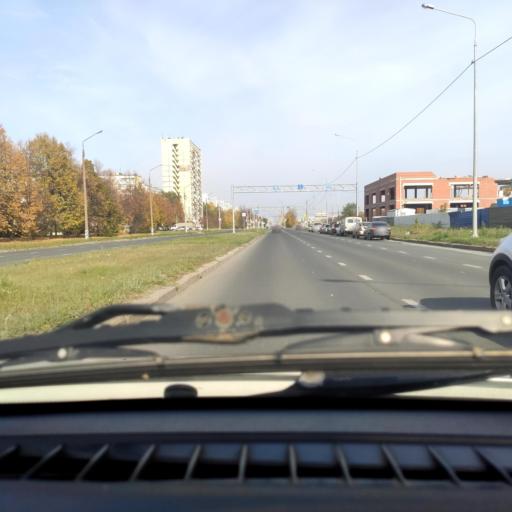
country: RU
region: Samara
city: Tol'yatti
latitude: 53.5054
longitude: 49.2704
